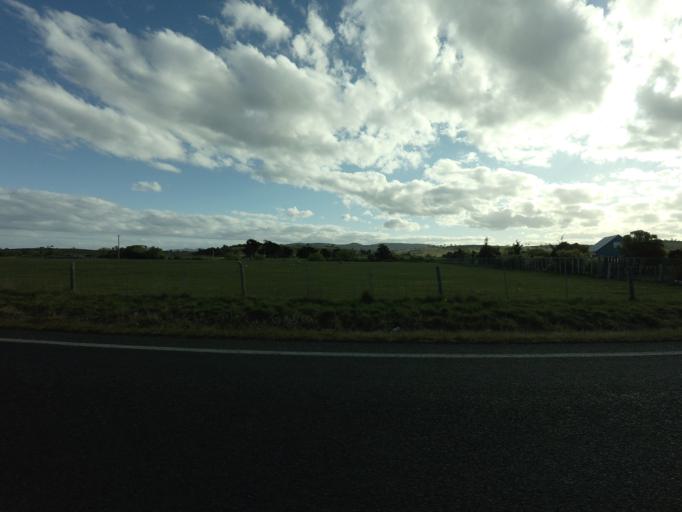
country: AU
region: Tasmania
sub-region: Sorell
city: Sorell
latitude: -42.7491
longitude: 147.5386
